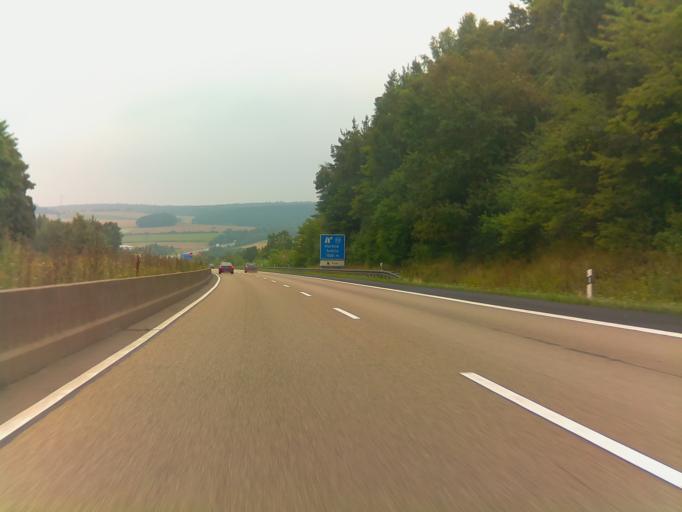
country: DE
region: Hesse
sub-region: Regierungsbezirk Kassel
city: Burghaun
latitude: 50.6485
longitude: 9.6825
